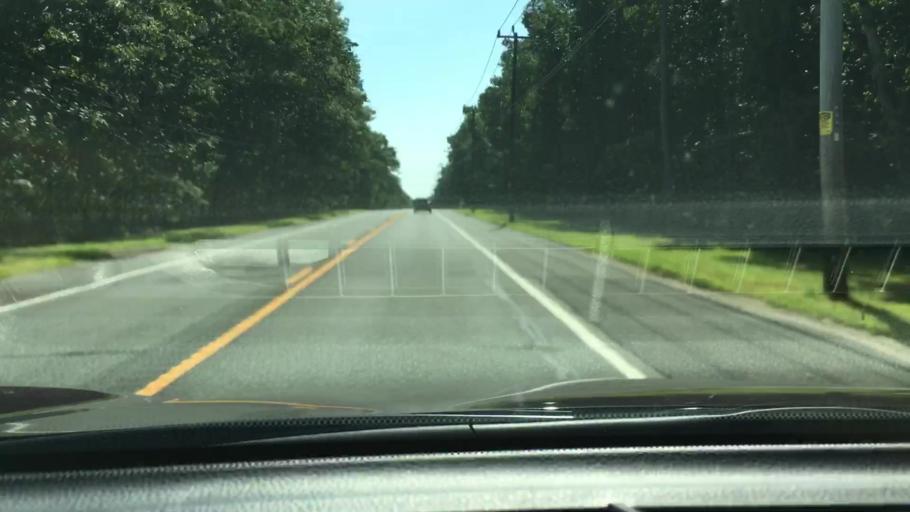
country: US
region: New Jersey
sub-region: Cumberland County
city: Millville
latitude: 39.3813
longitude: -74.9719
